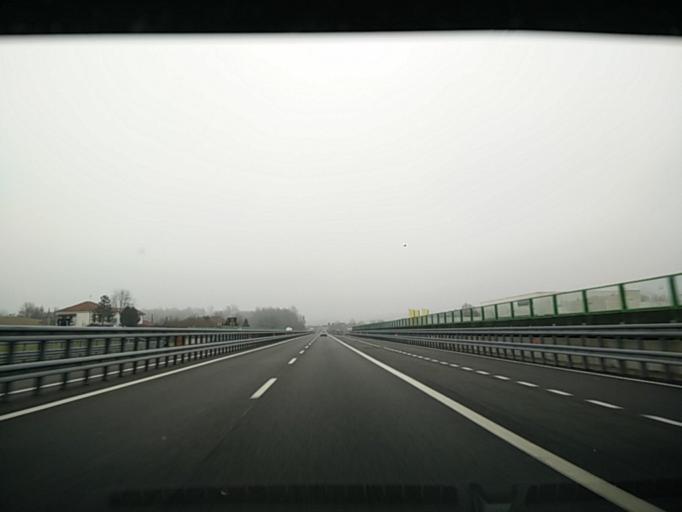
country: IT
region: Piedmont
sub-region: Provincia di Asti
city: Cantarana
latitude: 44.9084
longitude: 8.0503
